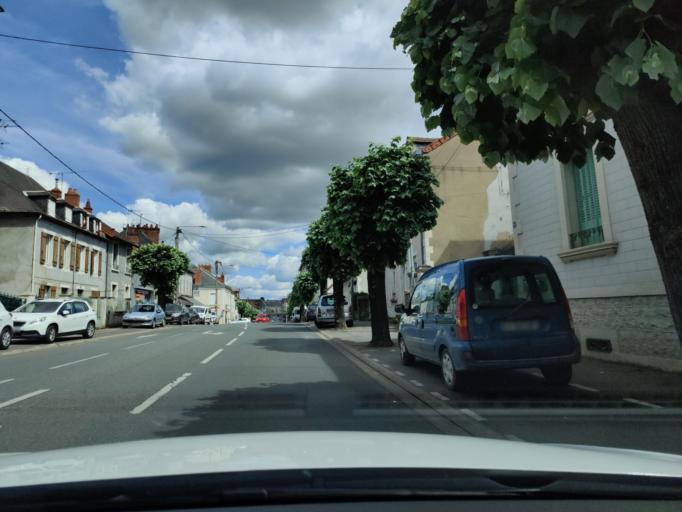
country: FR
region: Auvergne
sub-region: Departement de l'Allier
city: Montlucon
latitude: 46.3328
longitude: 2.6089
